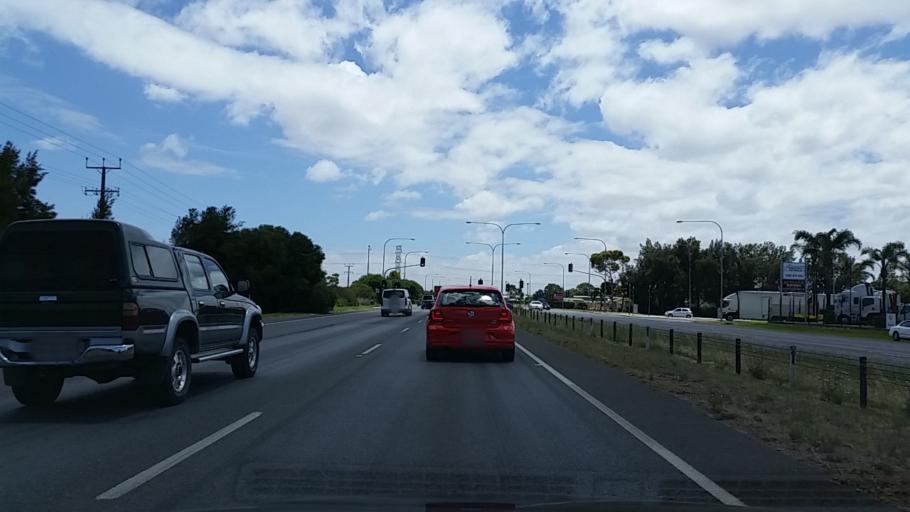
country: AU
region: South Australia
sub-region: Salisbury
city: Salisbury
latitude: -34.7894
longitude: 138.5963
